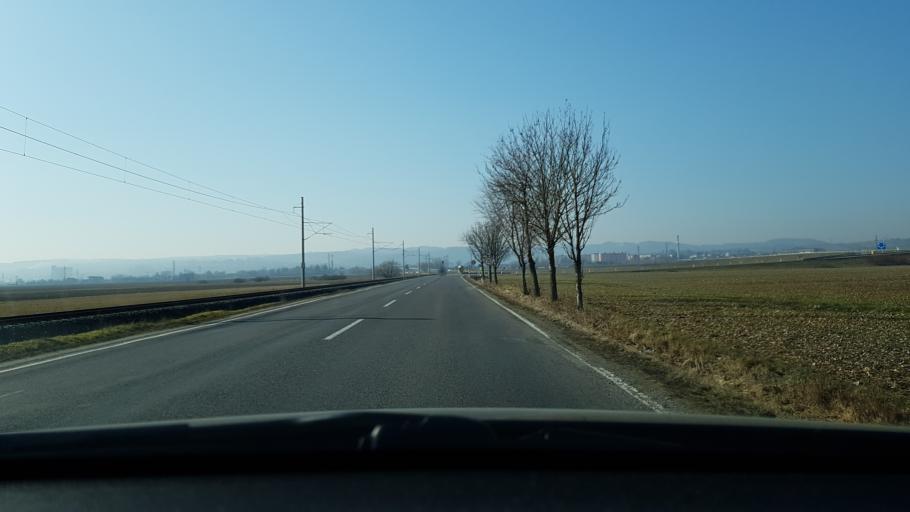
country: CZ
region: Olomoucky
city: Postrelmov
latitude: 49.8955
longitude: 16.9007
